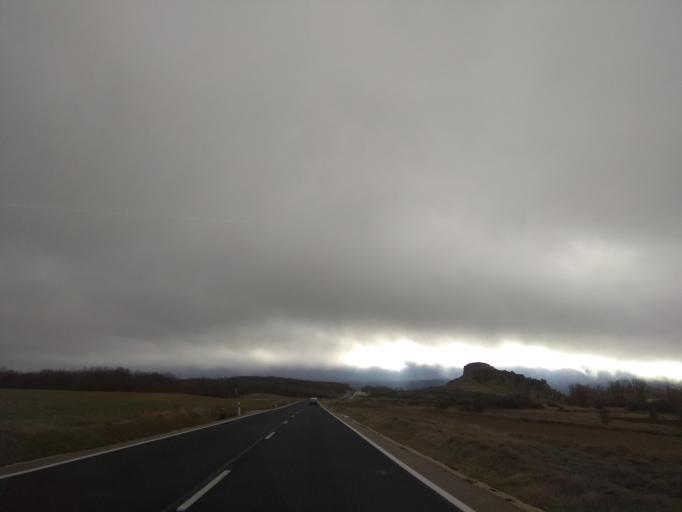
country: ES
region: Castille and Leon
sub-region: Provincia de Burgos
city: Tubilla del Agua
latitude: 42.6421
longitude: -3.8779
